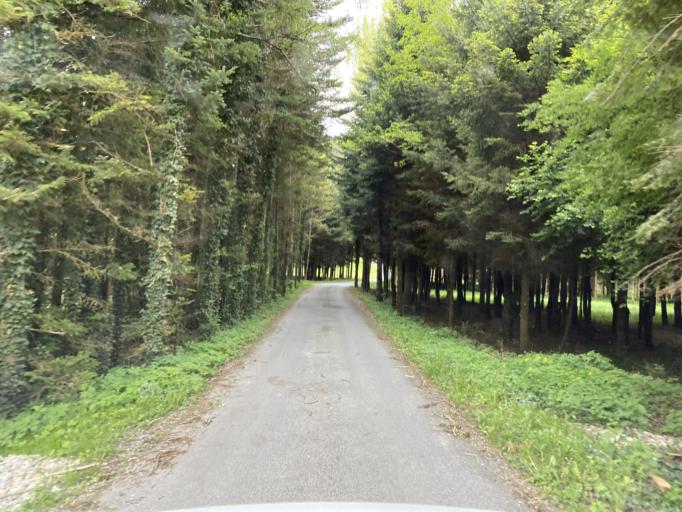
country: AT
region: Styria
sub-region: Politischer Bezirk Weiz
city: Koglhof
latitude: 47.3133
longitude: 15.6864
